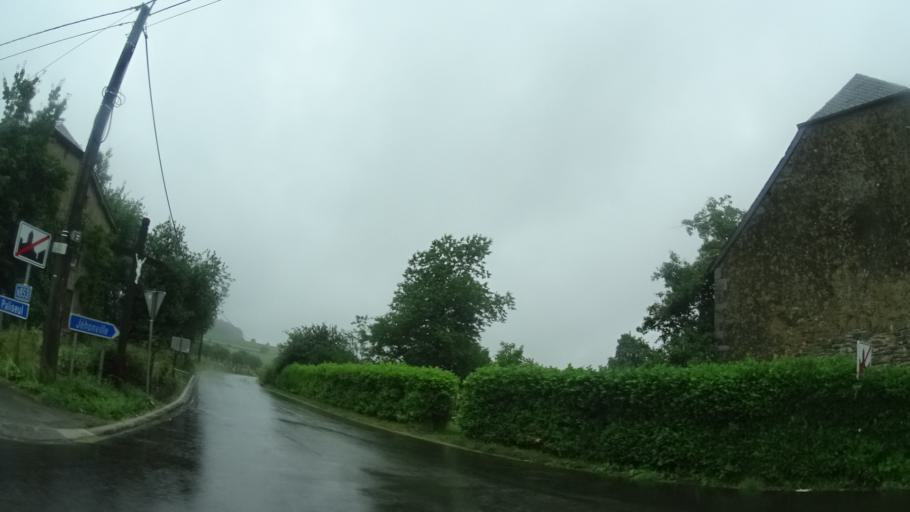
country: BE
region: Wallonia
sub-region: Province du Luxembourg
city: Bertrix
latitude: 49.8787
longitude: 5.2097
